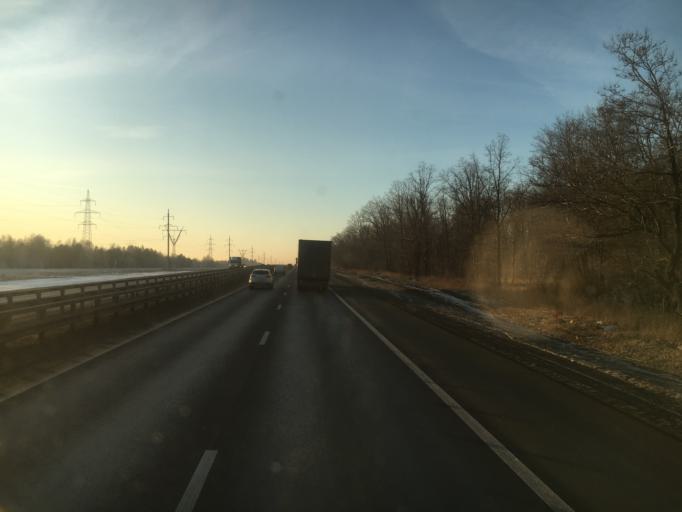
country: RU
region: Samara
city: Pribrezhnyy
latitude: 53.5186
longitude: 49.8108
